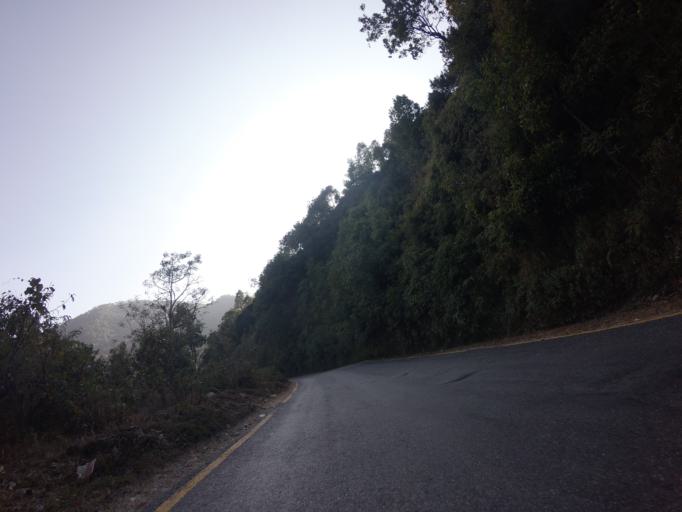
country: NP
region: Western Region
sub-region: Gandaki Zone
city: Pokhara
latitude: 28.1907
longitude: 83.9006
